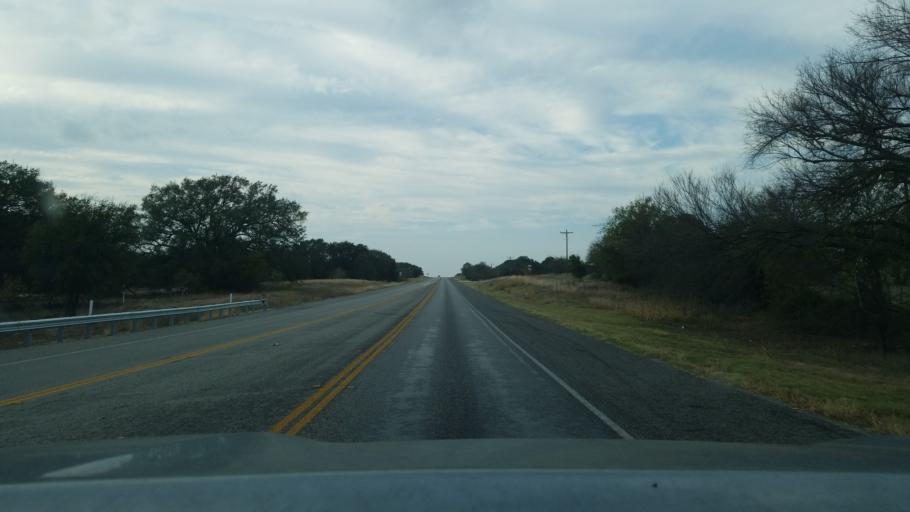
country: US
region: Texas
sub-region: Mills County
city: Goldthwaite
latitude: 31.5225
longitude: -98.5987
